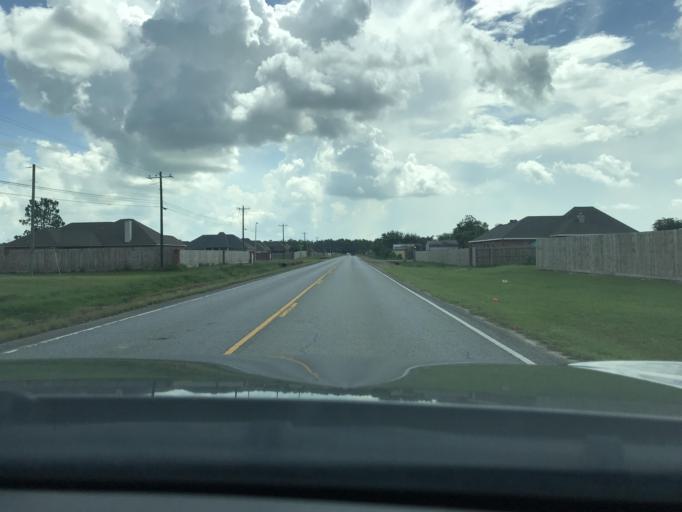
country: US
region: Louisiana
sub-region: Calcasieu Parish
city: Moss Bluff
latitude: 30.3408
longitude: -93.2420
